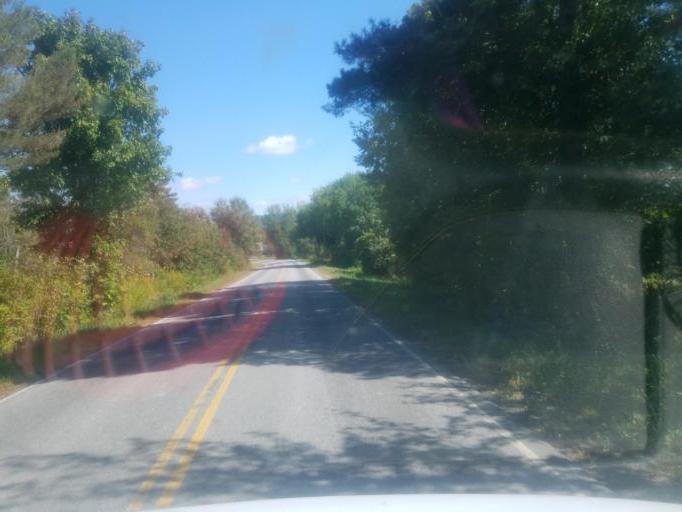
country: US
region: New York
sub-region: Allegany County
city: Friendship
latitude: 42.2758
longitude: -78.1423
